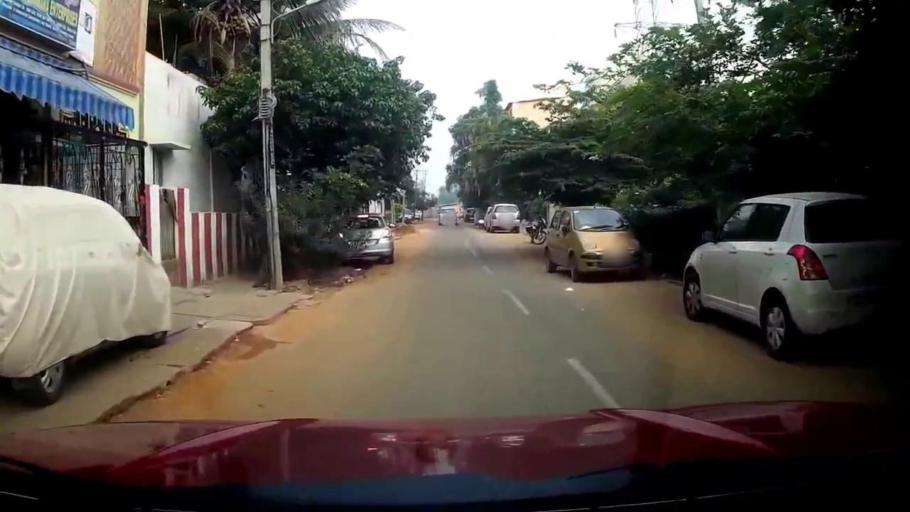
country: IN
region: Karnataka
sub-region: Bangalore Urban
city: Bangalore
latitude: 13.0364
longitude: 77.5662
